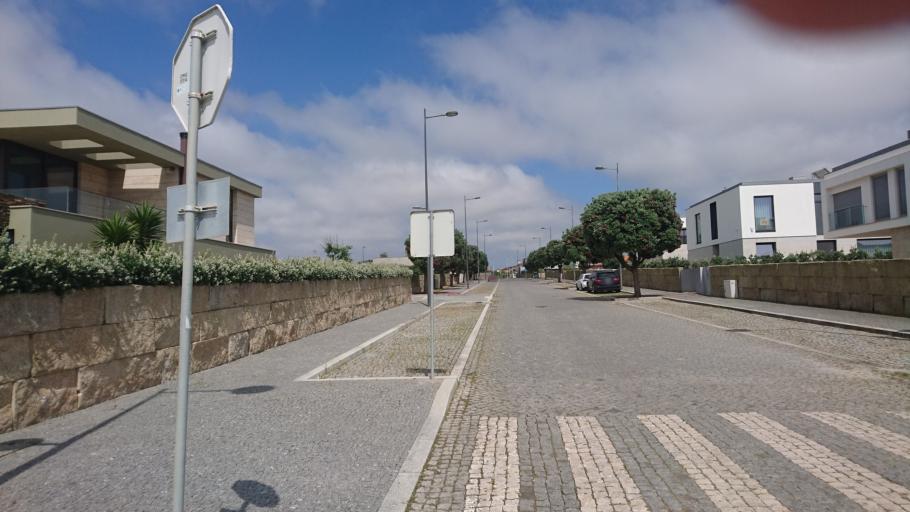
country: PT
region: Porto
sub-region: Matosinhos
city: Lavra
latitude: 41.2780
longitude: -8.7243
